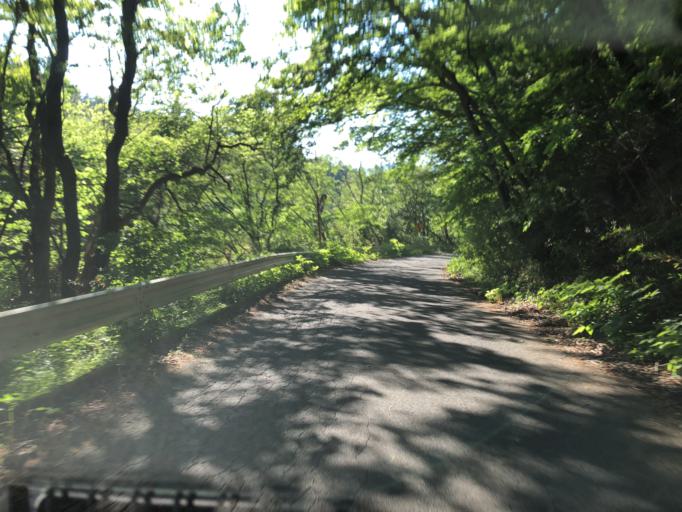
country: JP
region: Ibaraki
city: Kitaibaraki
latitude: 36.8762
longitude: 140.6661
